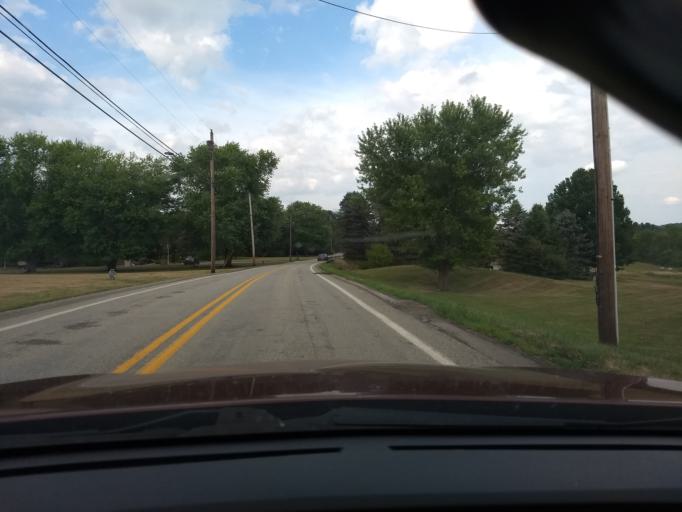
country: US
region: Pennsylvania
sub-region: Allegheny County
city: Curtisville
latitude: 40.6600
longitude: -79.8631
